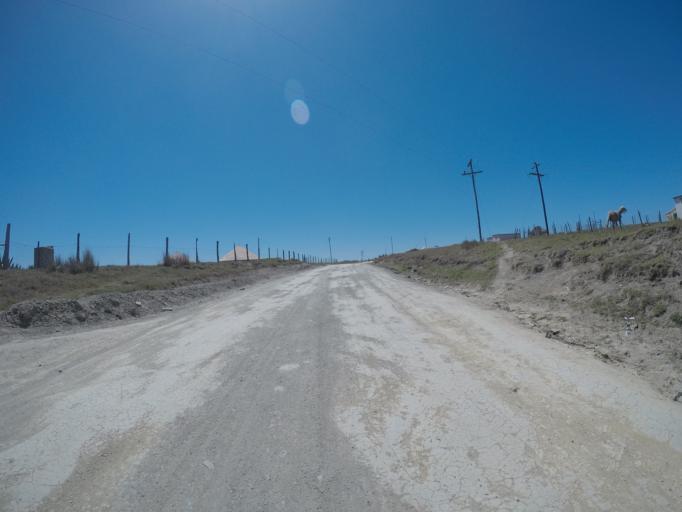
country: ZA
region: Eastern Cape
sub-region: OR Tambo District Municipality
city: Libode
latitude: -31.9396
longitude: 29.0277
